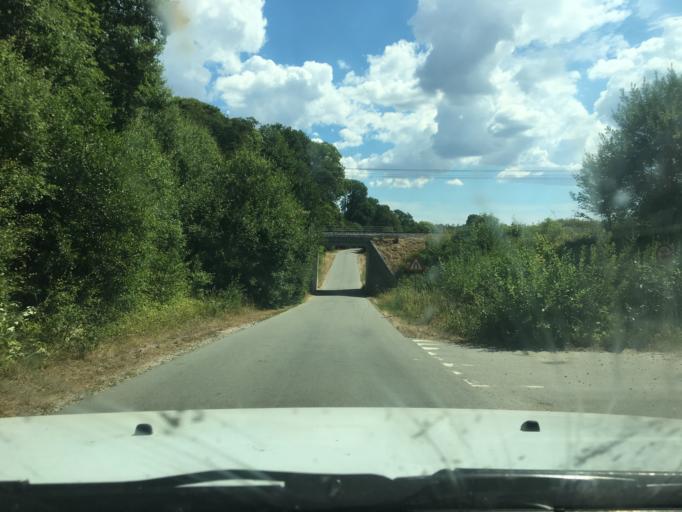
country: DK
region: Central Jutland
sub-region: Syddjurs Kommune
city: Hornslet
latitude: 56.3348
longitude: 10.3232
